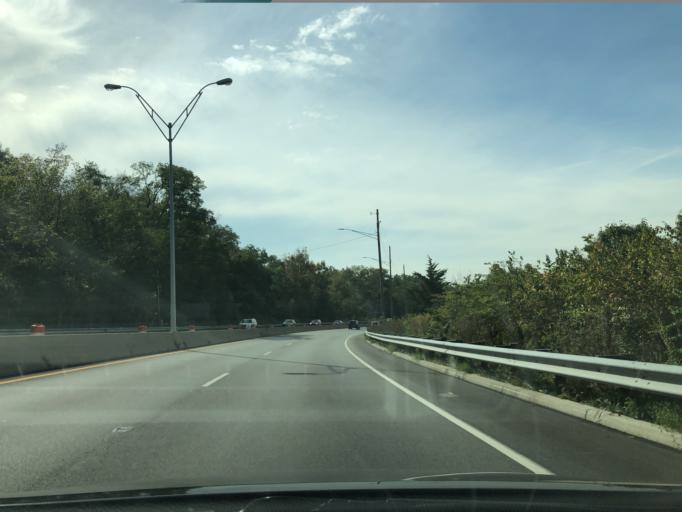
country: US
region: Ohio
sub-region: Hamilton County
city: Fairfax
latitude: 39.1688
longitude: -84.3981
